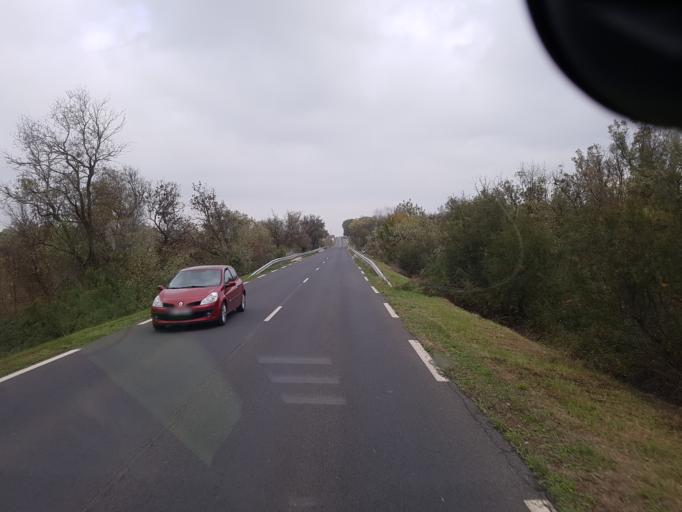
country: FR
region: Languedoc-Roussillon
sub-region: Departement de l'Herault
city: Marseillan
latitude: 43.3838
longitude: 3.5360
